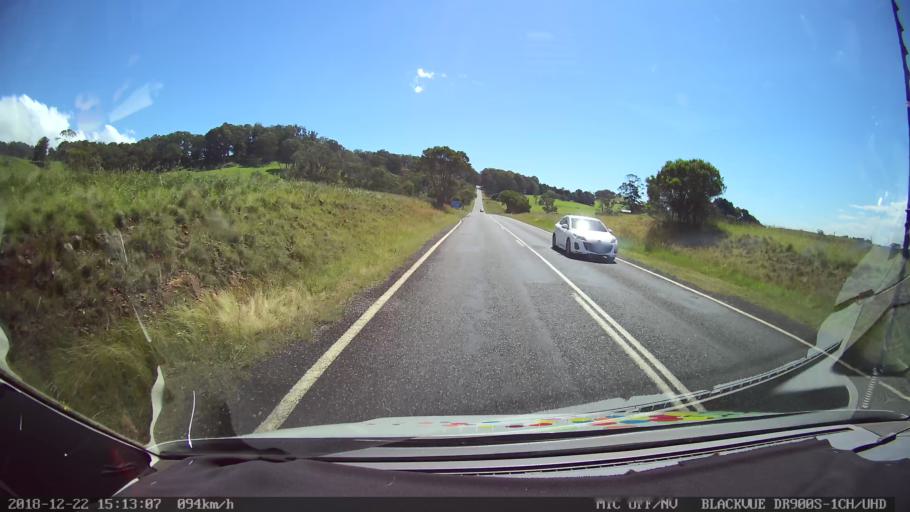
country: AU
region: New South Wales
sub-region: Bellingen
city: Dorrigo
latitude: -30.3606
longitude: 152.3923
